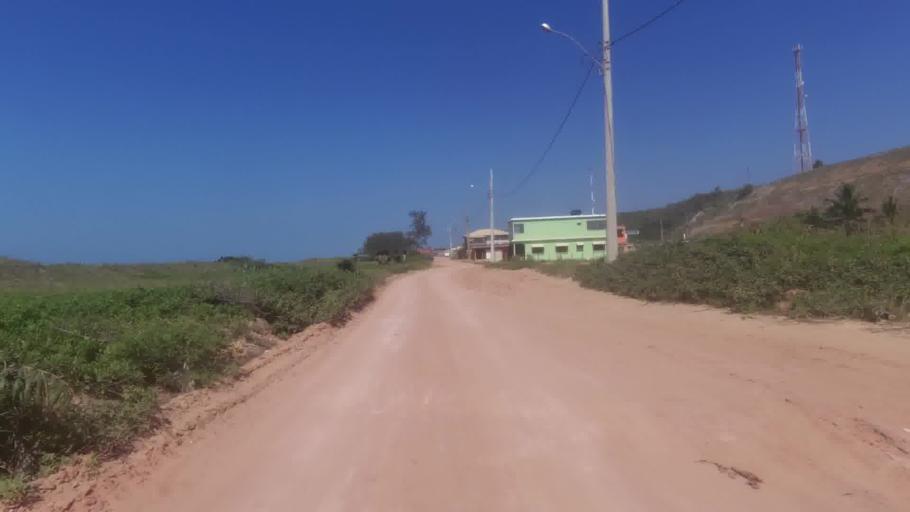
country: BR
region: Espirito Santo
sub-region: Marataizes
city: Marataizes
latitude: -21.1008
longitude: -40.8489
